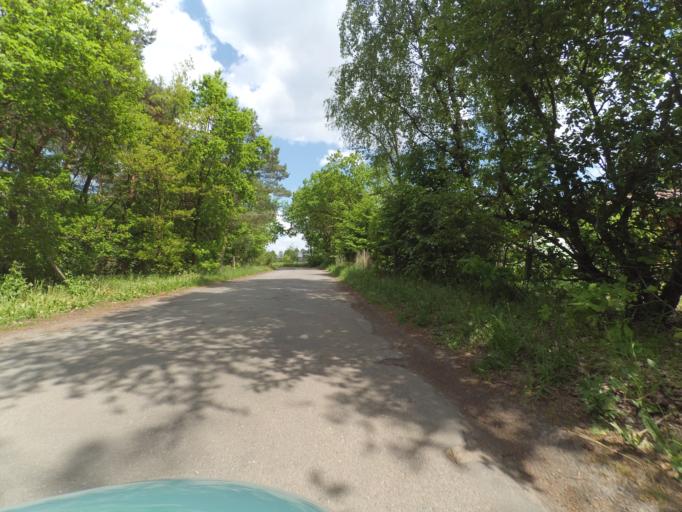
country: DE
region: Lower Saxony
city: Wienhausen
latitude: 52.5874
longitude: 10.2203
